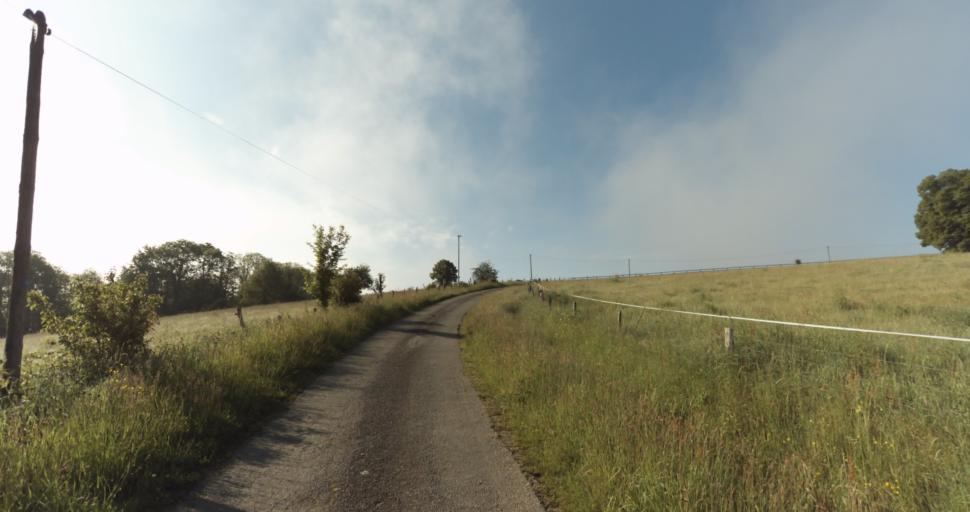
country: FR
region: Limousin
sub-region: Departement de la Haute-Vienne
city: Le Vigen
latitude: 45.7486
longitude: 1.2843
